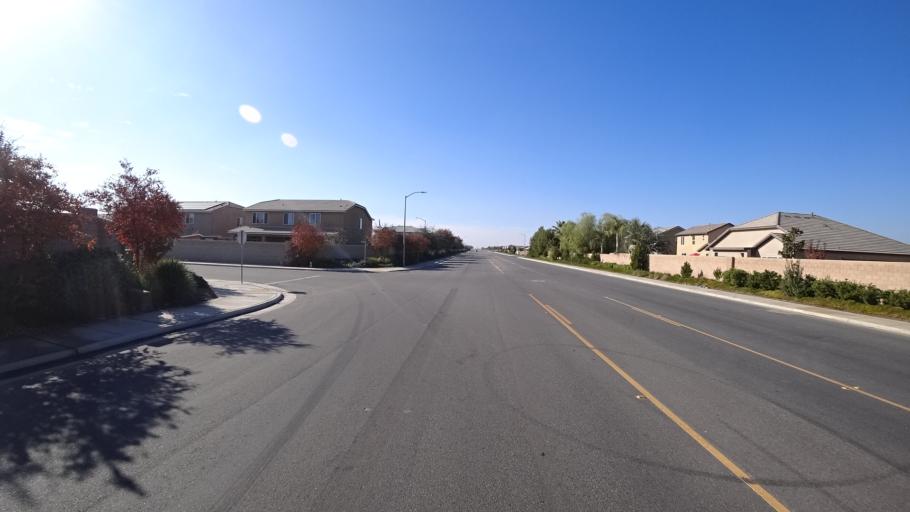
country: US
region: California
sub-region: Kern County
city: Greenfield
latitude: 35.2887
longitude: -119.0590
